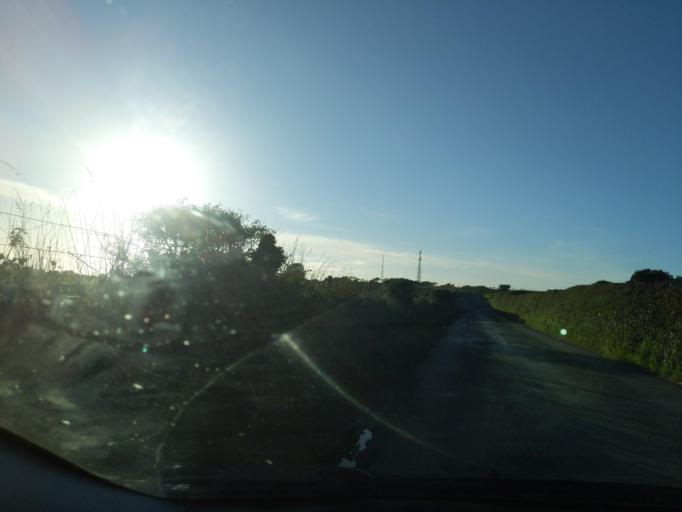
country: GB
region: England
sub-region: Plymouth
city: Plymstock
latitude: 50.3452
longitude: -4.1029
